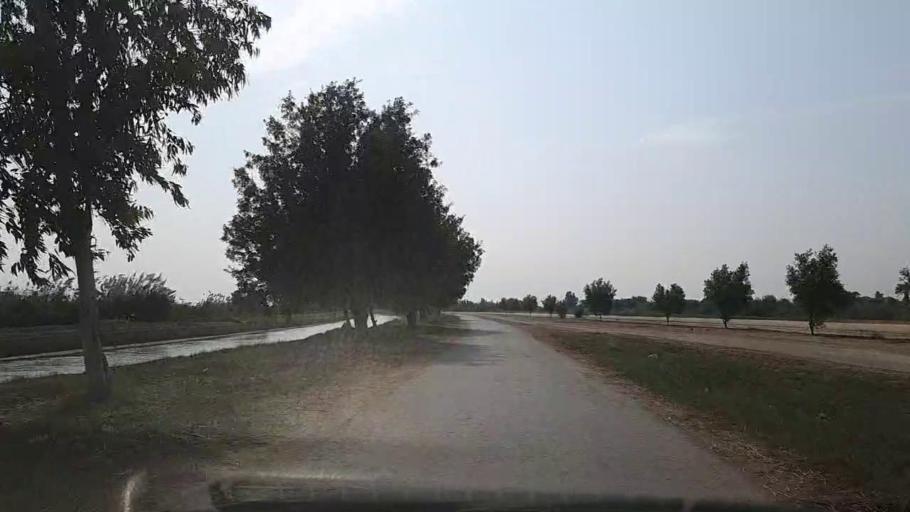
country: PK
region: Sindh
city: Thatta
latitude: 24.7462
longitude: 67.7675
